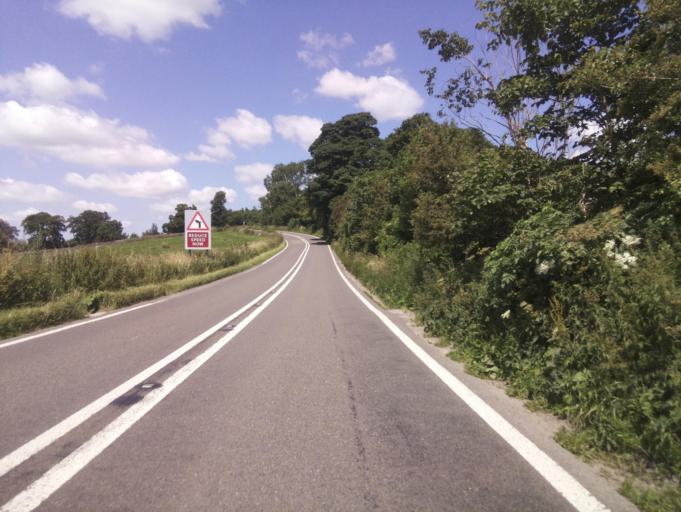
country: GB
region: England
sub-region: Derbyshire
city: Ashbourne
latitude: 53.0685
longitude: -1.7484
